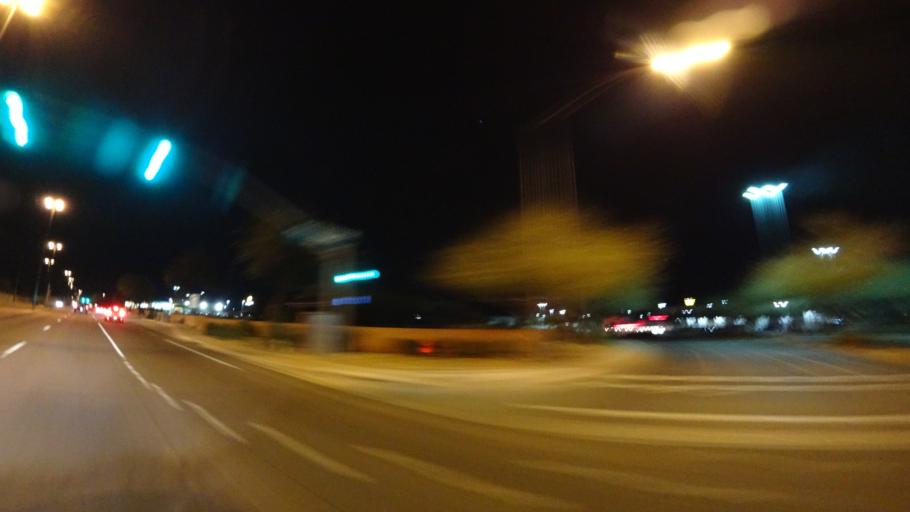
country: US
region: Arizona
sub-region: Maricopa County
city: Gilbert
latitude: 33.3939
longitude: -111.6934
